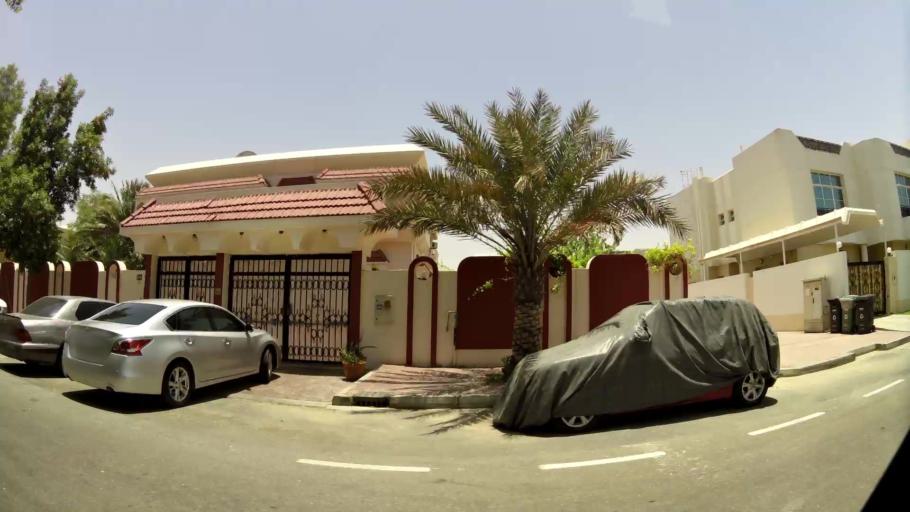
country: AE
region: Dubai
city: Dubai
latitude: 25.1781
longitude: 55.2316
